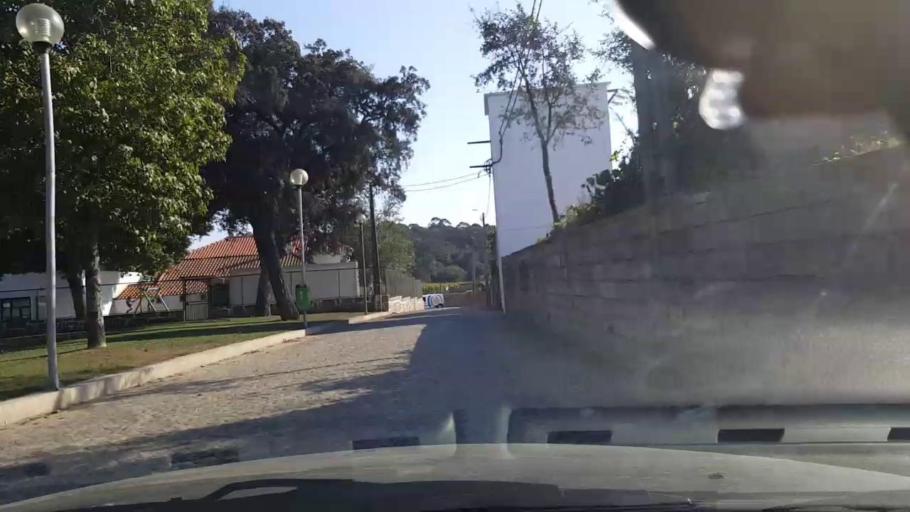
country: PT
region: Porto
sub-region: Vila do Conde
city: Arvore
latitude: 41.3505
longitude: -8.7184
